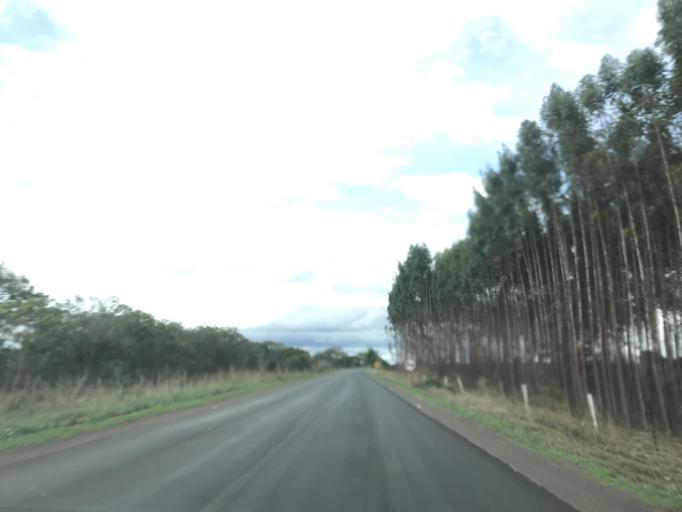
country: BR
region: Goias
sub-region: Bela Vista De Goias
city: Bela Vista de Goias
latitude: -16.9846
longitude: -48.6683
